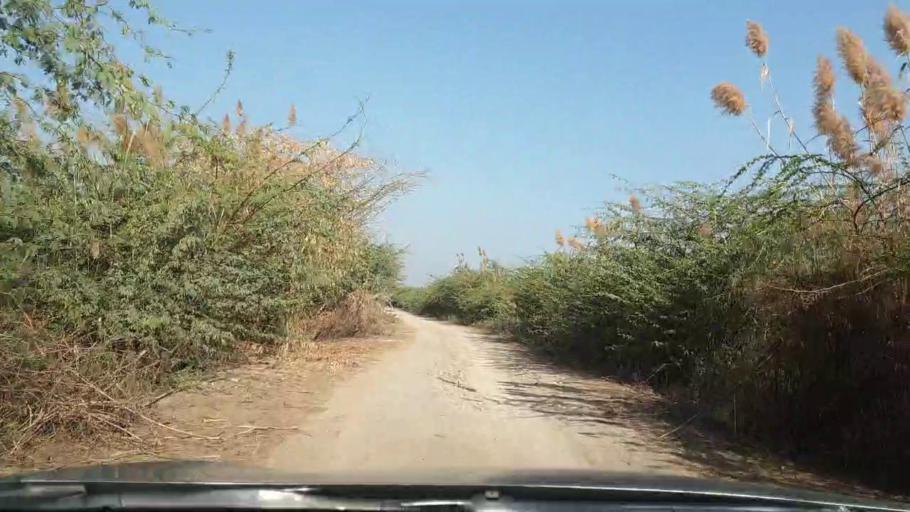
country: PK
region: Sindh
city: Mirpur Khas
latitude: 25.6559
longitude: 68.9132
